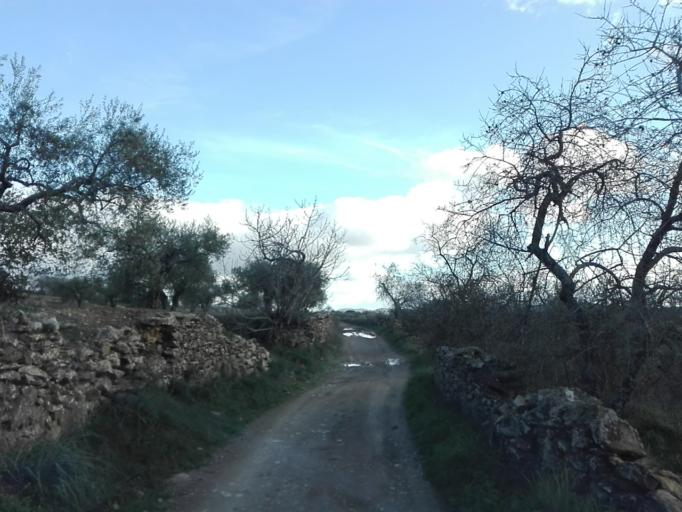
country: ES
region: Extremadura
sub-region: Provincia de Badajoz
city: Trasierra
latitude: 38.1870
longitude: -5.9894
